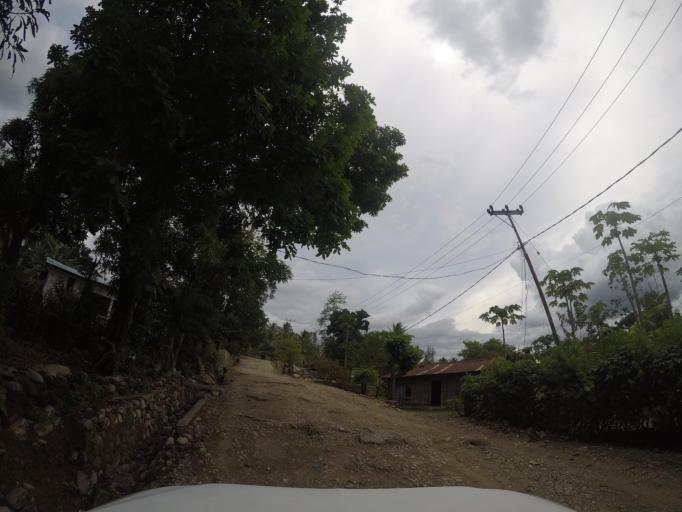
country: TL
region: Bobonaro
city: Maliana
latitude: -8.9936
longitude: 125.2182
